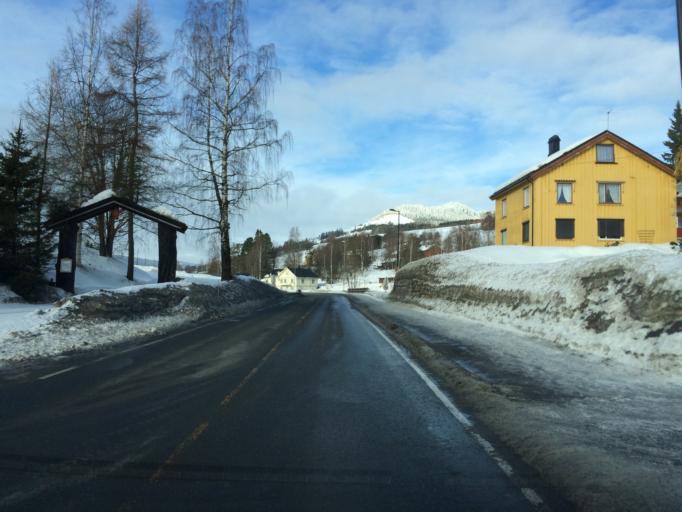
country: NO
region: Oppland
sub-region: Gausdal
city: Segalstad bru
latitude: 61.2182
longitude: 10.2766
